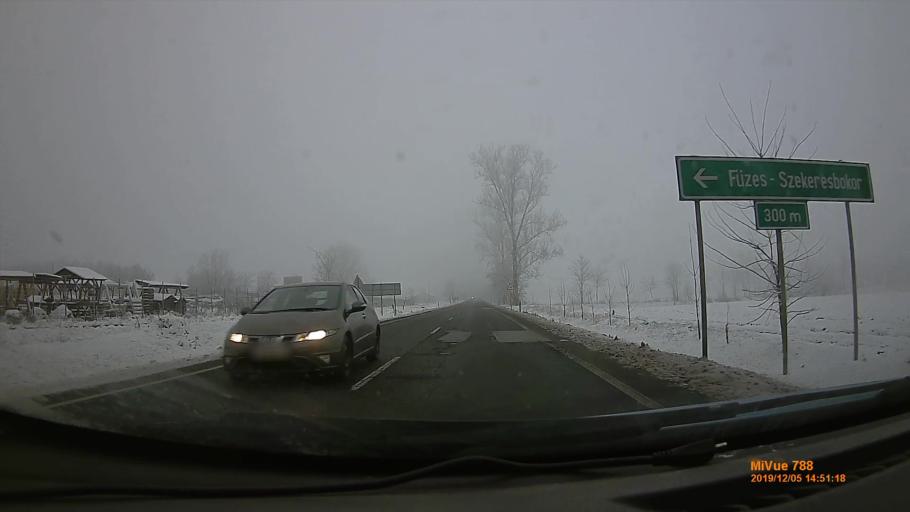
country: HU
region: Szabolcs-Szatmar-Bereg
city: Nyirtelek
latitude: 47.9923
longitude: 21.6597
